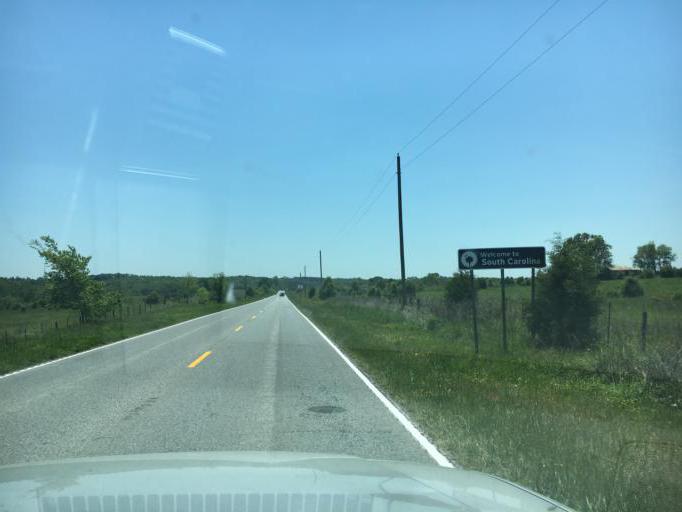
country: US
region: South Carolina
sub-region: Cherokee County
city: Blacksburg
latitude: 35.1707
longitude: -81.5732
